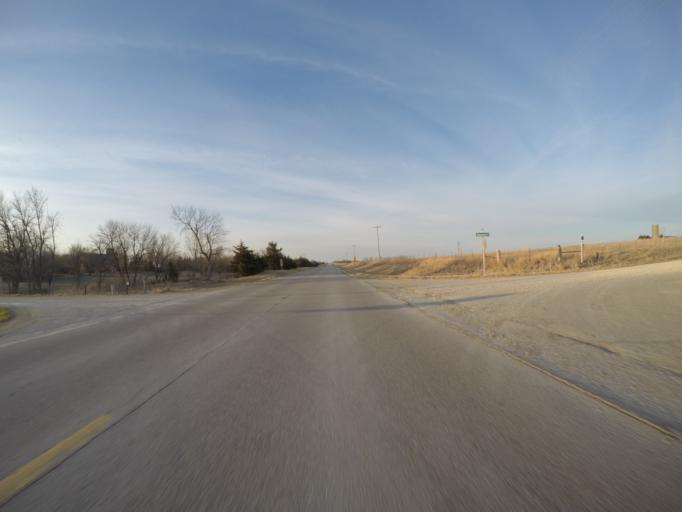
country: US
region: Kansas
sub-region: Riley County
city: Fort Riley North
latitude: 39.3205
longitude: -96.8307
